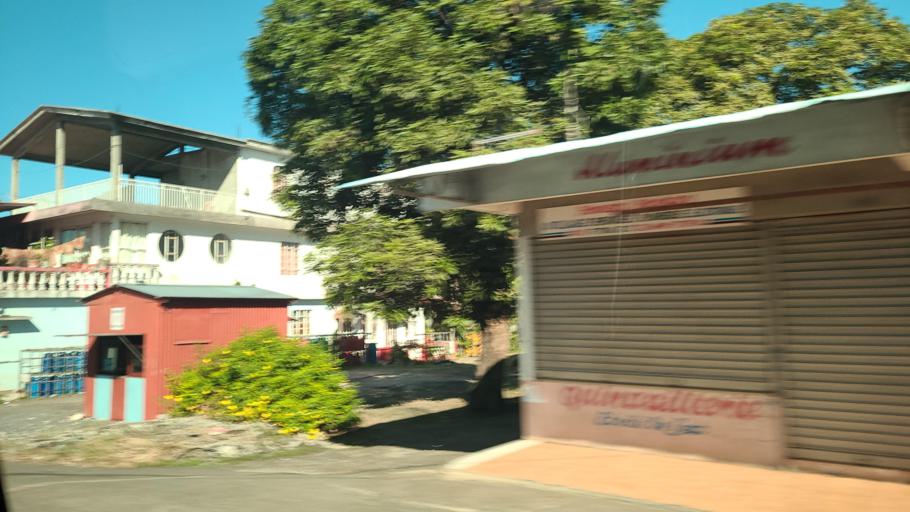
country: MU
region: Flacq
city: Poste de Flacq
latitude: -20.1698
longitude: 57.7326
